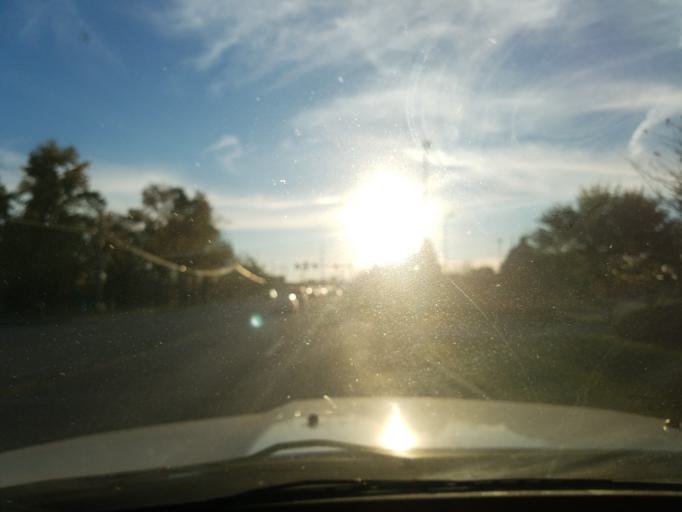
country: US
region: Indiana
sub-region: Clark County
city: Clarksville
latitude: 38.3212
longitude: -85.7494
